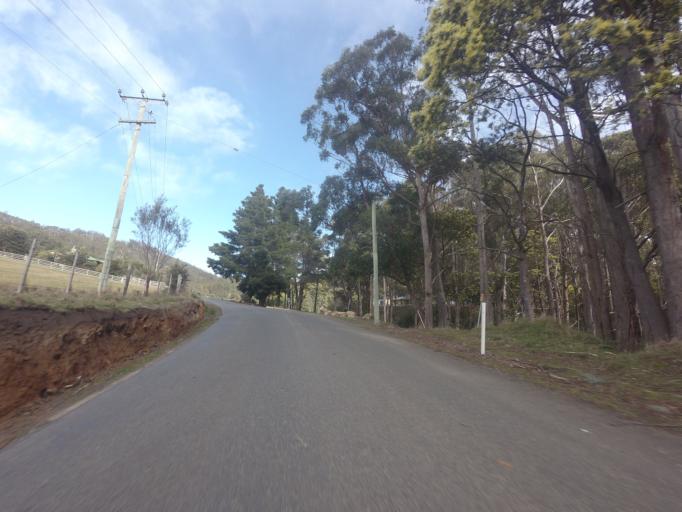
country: AU
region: Tasmania
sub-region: Kingborough
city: Margate
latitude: -42.9977
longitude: 147.1786
